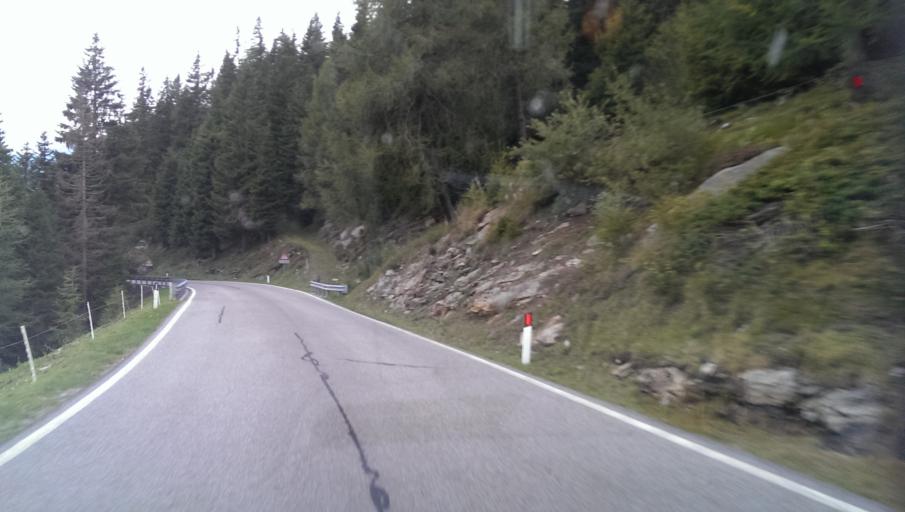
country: IT
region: Trentino-Alto Adige
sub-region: Bolzano
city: Racines
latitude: 46.8338
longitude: 11.3121
